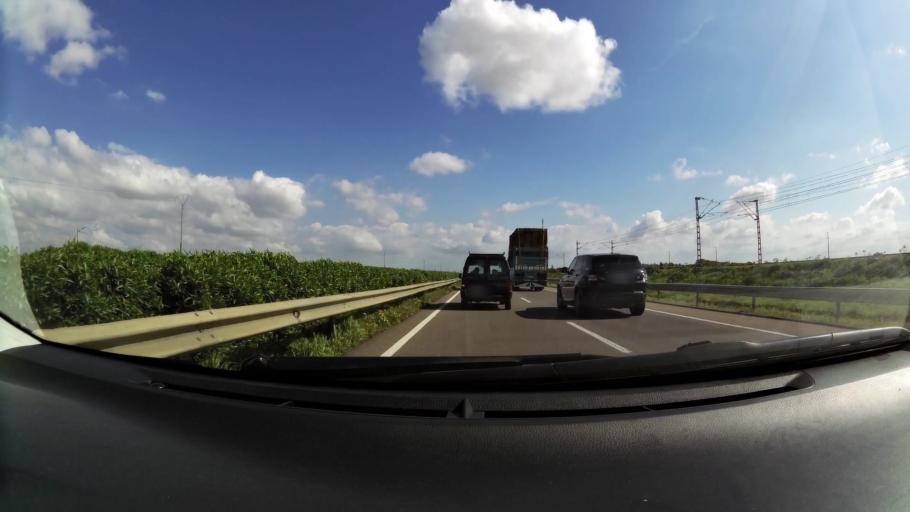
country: MA
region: Chaouia-Ouardigha
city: Nouaseur
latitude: 33.3464
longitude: -7.6143
